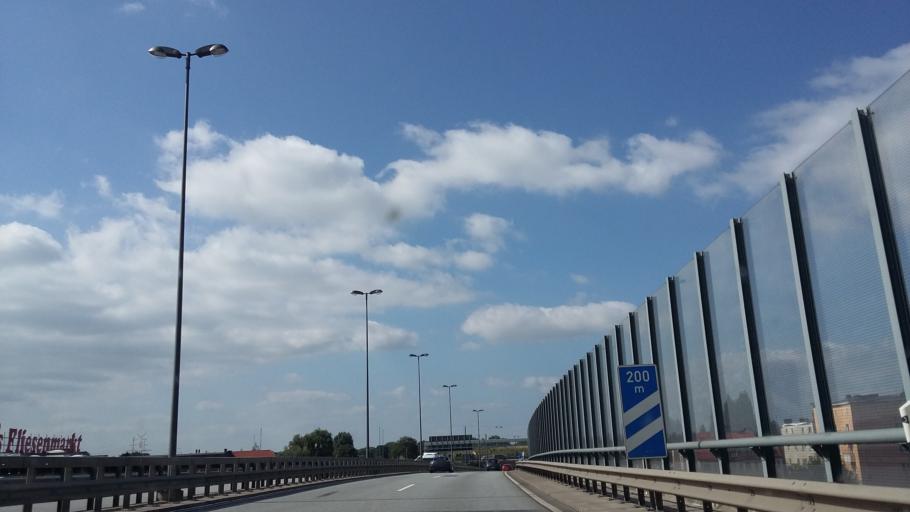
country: DE
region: Bremen
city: Bremen
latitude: 53.0638
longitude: 8.7804
